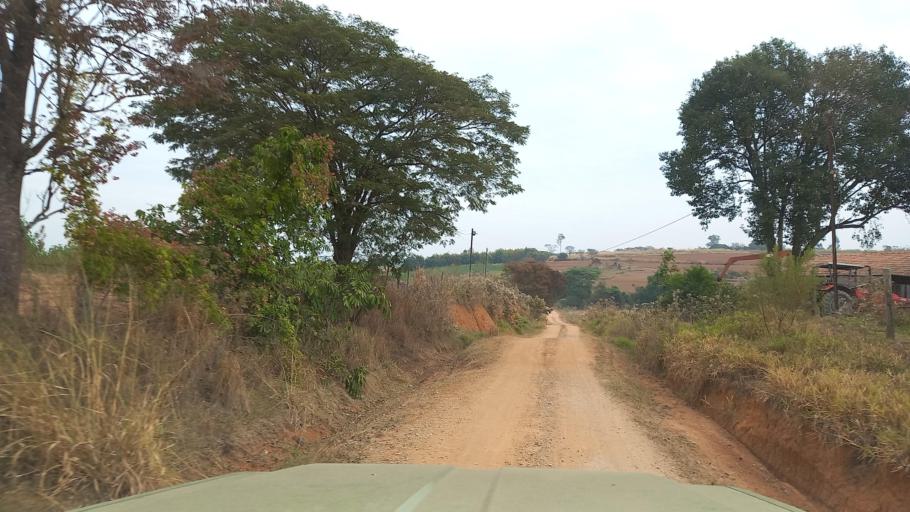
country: BR
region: Sao Paulo
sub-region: Moji-Guacu
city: Mogi-Gaucu
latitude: -22.2732
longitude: -46.8359
